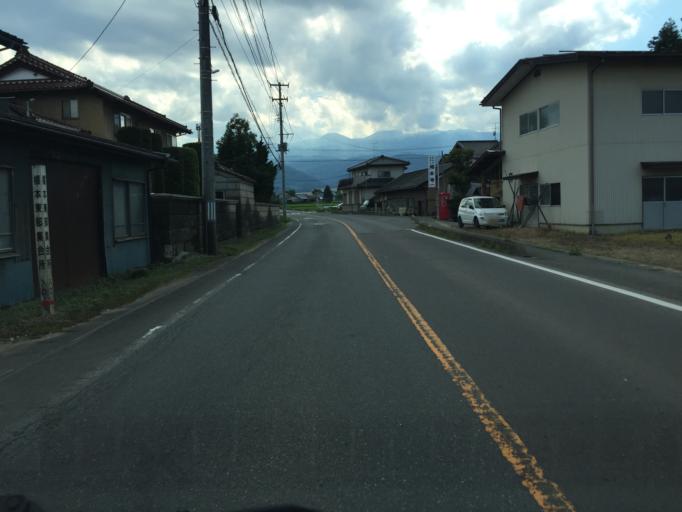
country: JP
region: Fukushima
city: Fukushima-shi
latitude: 37.7480
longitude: 140.4007
